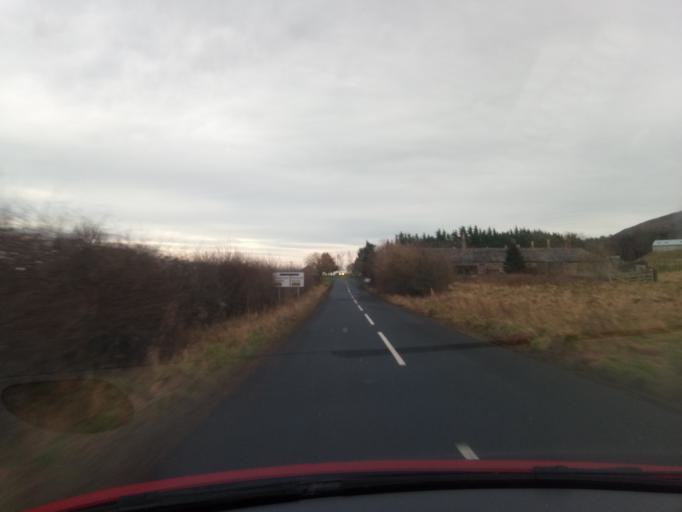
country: GB
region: England
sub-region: Northumberland
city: Kirknewton
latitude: 55.5613
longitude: -2.0724
